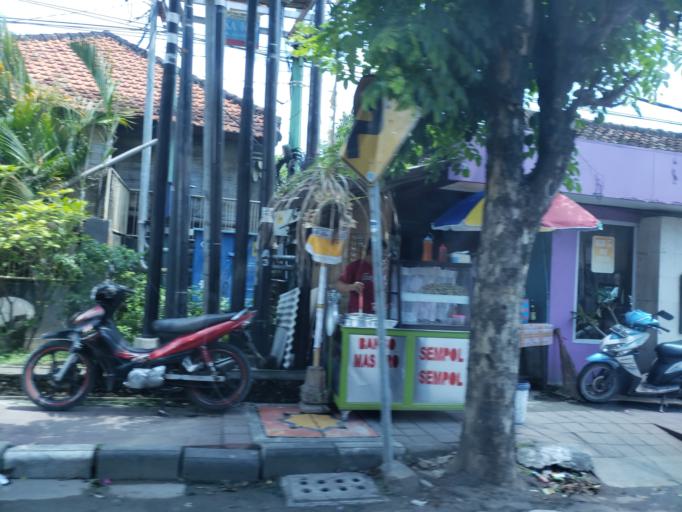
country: ID
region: Bali
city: Jimbaran
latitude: -8.7769
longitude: 115.1707
